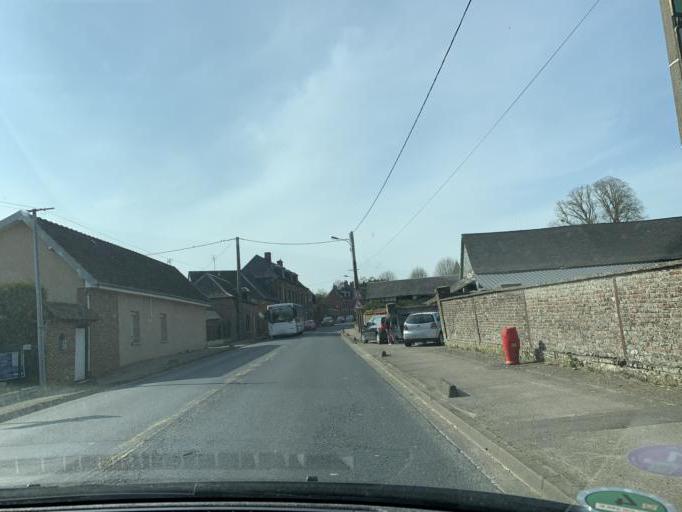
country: FR
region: Haute-Normandie
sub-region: Departement de l'Eure
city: Les Andelys
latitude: 49.3085
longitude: 1.4356
